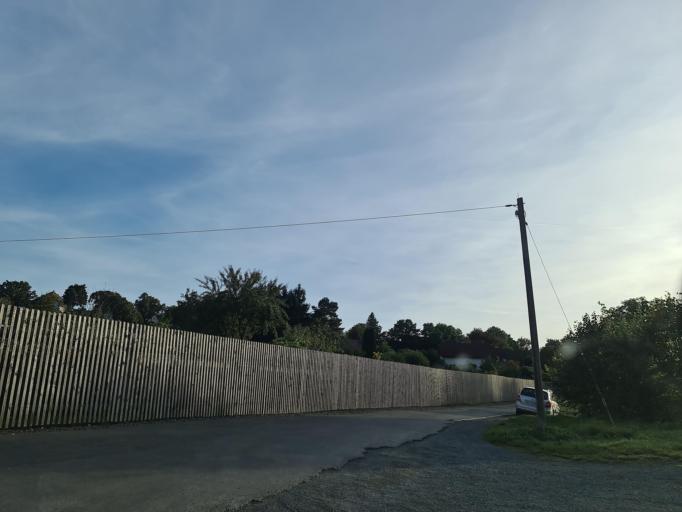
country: DE
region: Saxony
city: Plauen
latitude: 50.4999
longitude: 12.1178
